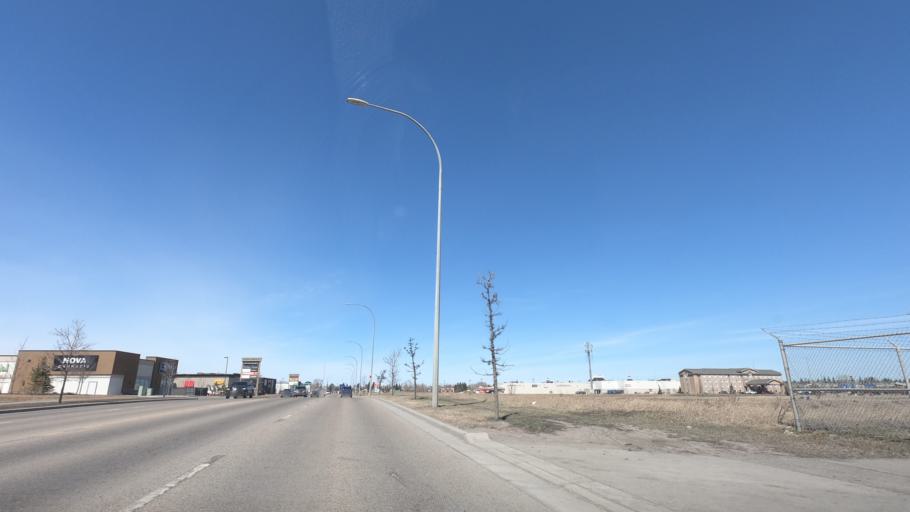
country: CA
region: Alberta
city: Airdrie
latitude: 51.2658
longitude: -114.0066
